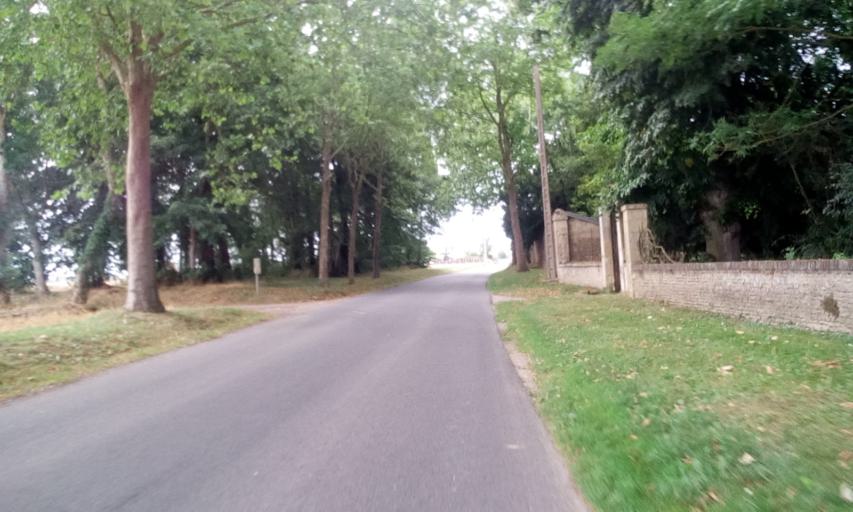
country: FR
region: Lower Normandy
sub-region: Departement du Calvados
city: Bellengreville
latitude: 49.1080
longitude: -0.2050
